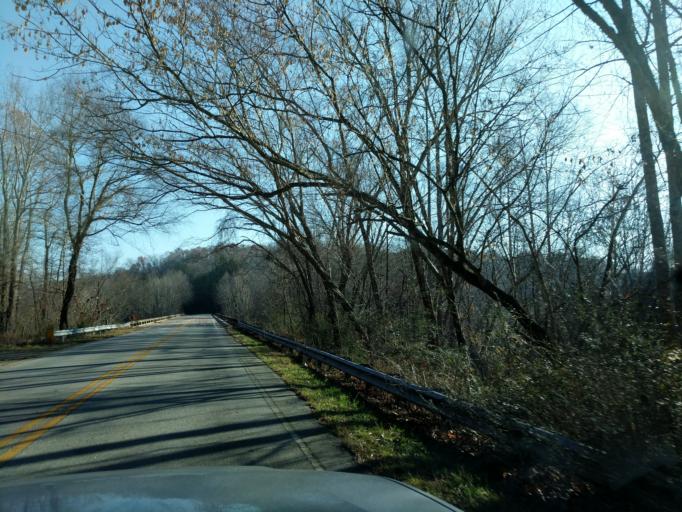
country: US
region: North Carolina
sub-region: Rutherford County
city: Rutherfordton
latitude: 35.2888
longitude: -81.9980
